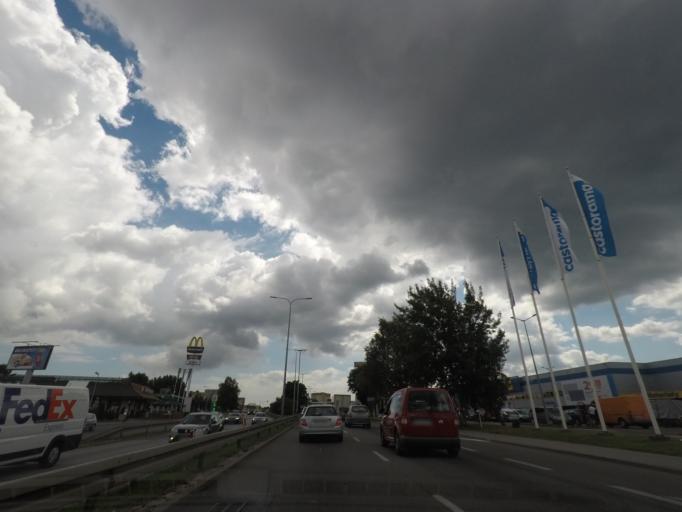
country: PL
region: Pomeranian Voivodeship
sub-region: Powiat wejherowski
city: Rumia
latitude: 54.5724
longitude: 18.3845
